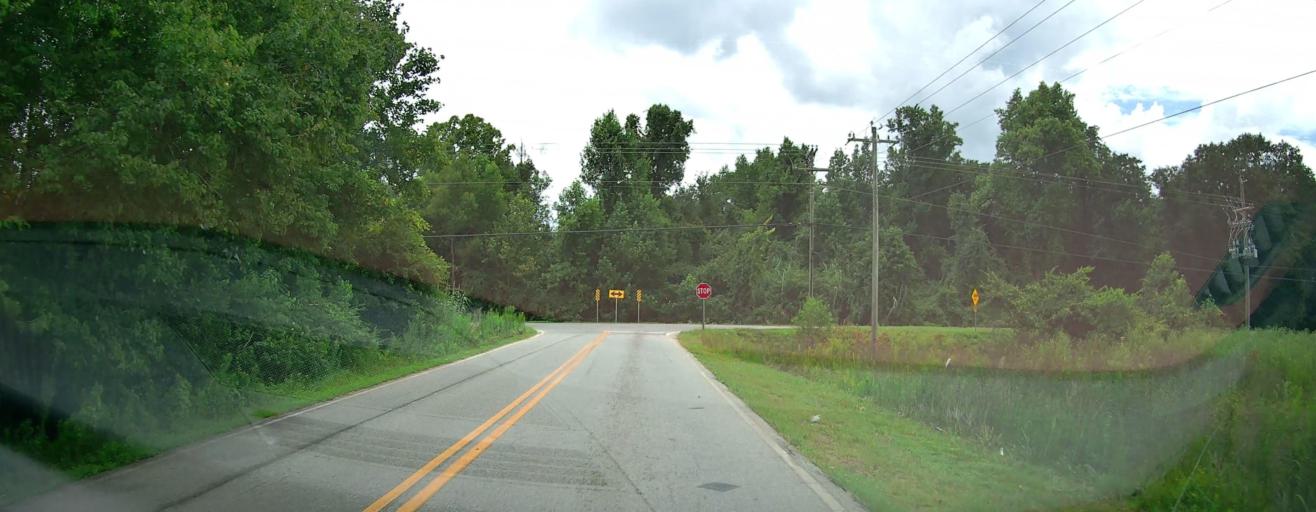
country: US
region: Georgia
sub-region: Houston County
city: Perry
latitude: 32.5469
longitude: -83.7534
